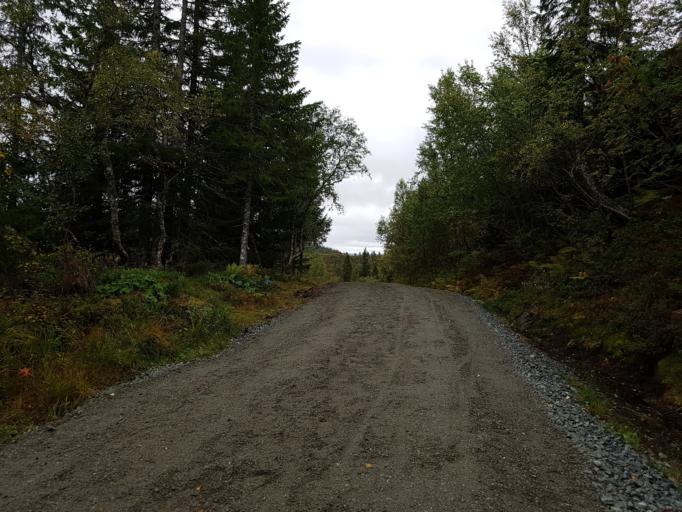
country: NO
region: Sor-Trondelag
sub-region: Melhus
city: Melhus
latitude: 63.4179
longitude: 10.2259
